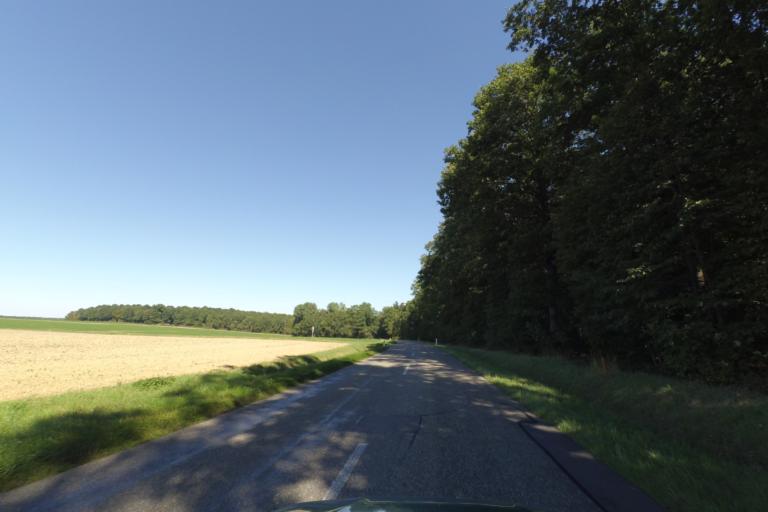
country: DE
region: Baden-Wuerttemberg
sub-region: Regierungsbezirk Stuttgart
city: Schrozberg
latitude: 49.3380
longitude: 9.9487
